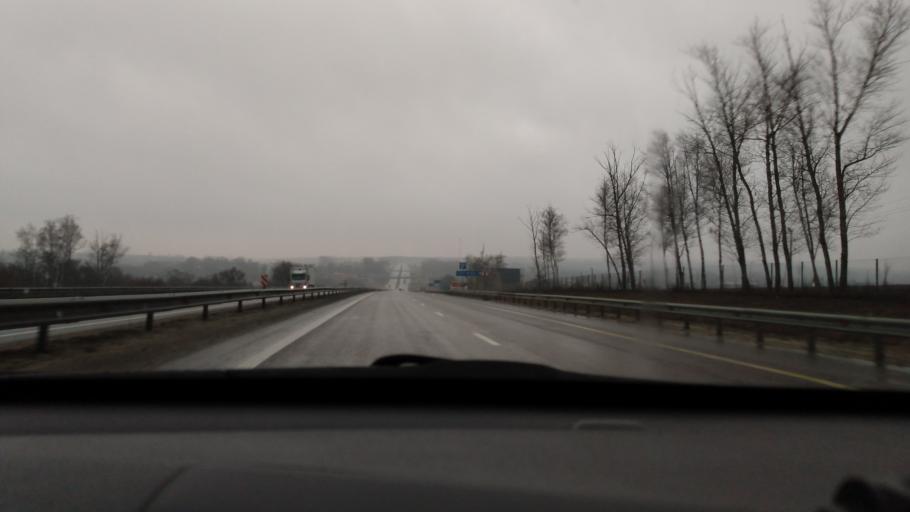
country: RU
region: Tula
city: Shvartsevskiy
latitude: 54.1223
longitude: 38.0575
